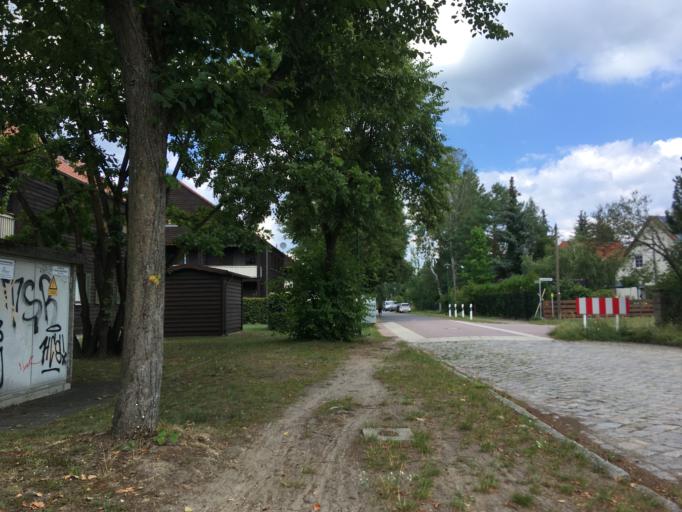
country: DE
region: Berlin
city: Buch
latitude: 52.6704
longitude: 13.5246
